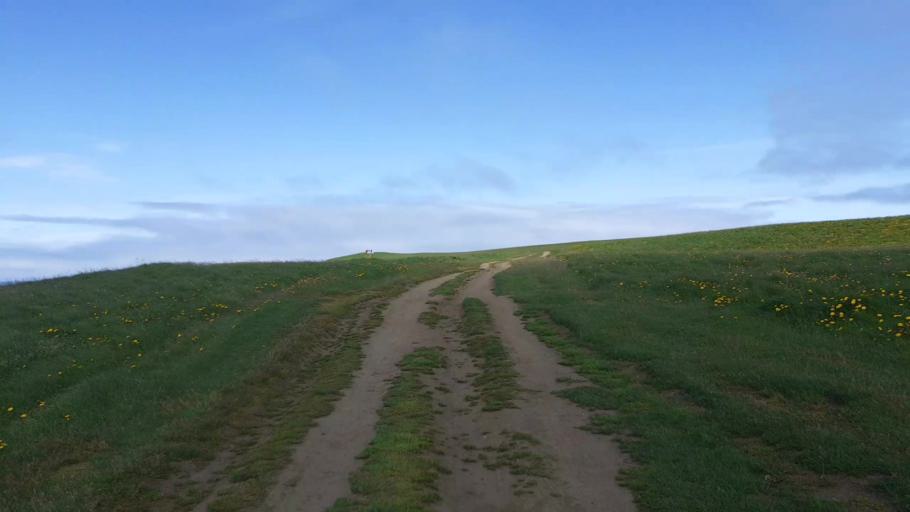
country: IS
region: Northeast
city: Dalvik
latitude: 66.5550
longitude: -18.0119
